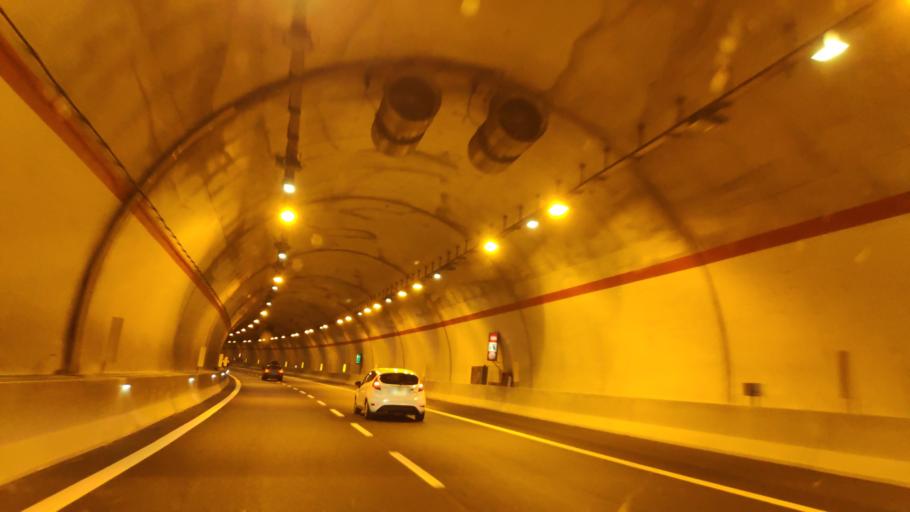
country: IT
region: Calabria
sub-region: Provincia di Cosenza
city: Laino Borgo
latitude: 39.9444
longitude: 15.9592
